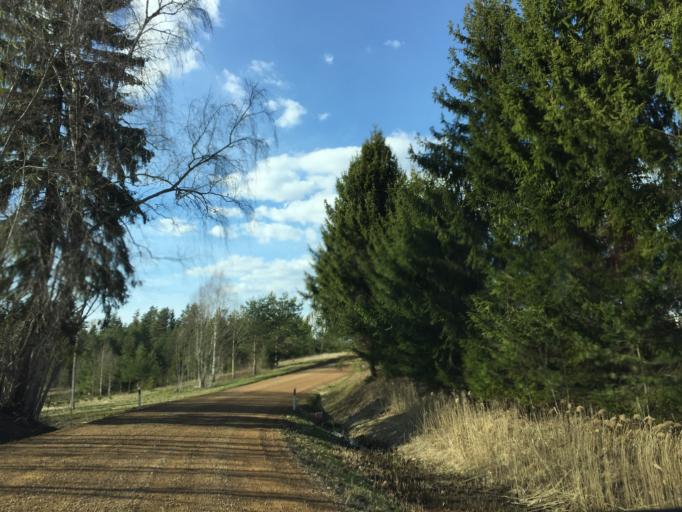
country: EE
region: Tartu
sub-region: Elva linn
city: Elva
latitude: 58.0900
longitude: 26.5138
